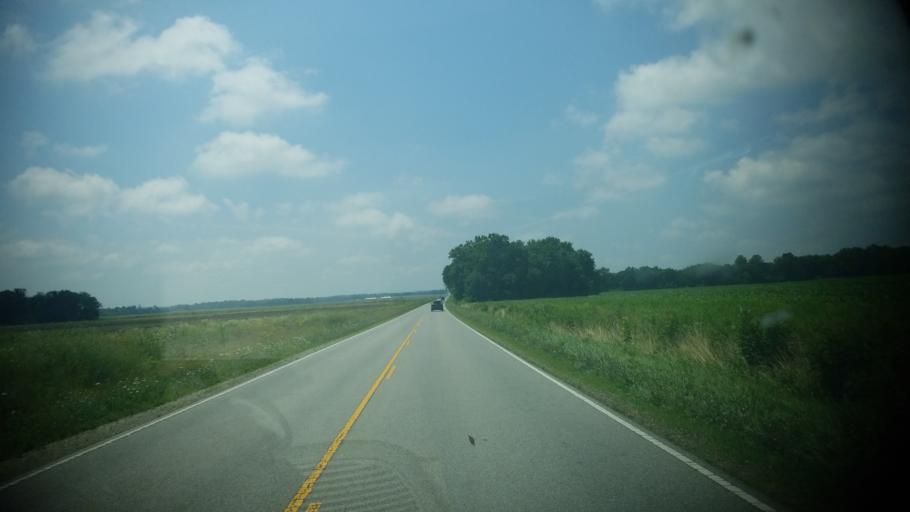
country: US
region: Illinois
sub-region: Wayne County
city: Fairfield
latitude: 38.4659
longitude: -88.3490
